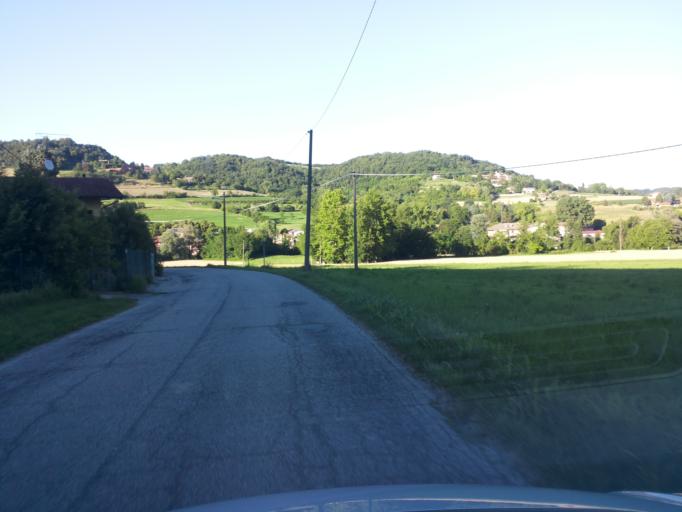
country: IT
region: Piedmont
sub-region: Provincia di Alessandria
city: Murisengo
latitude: 45.0841
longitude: 8.1453
